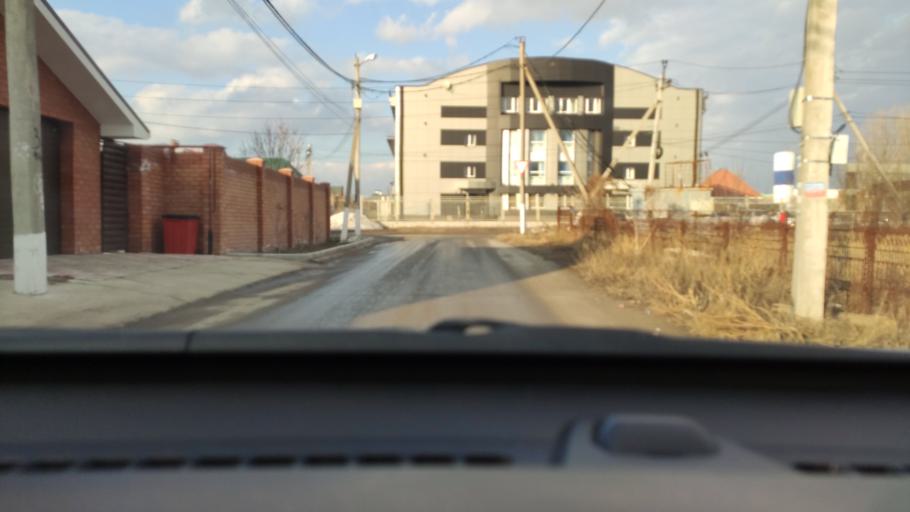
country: RU
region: Samara
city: Podstepki
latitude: 53.5092
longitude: 49.2399
